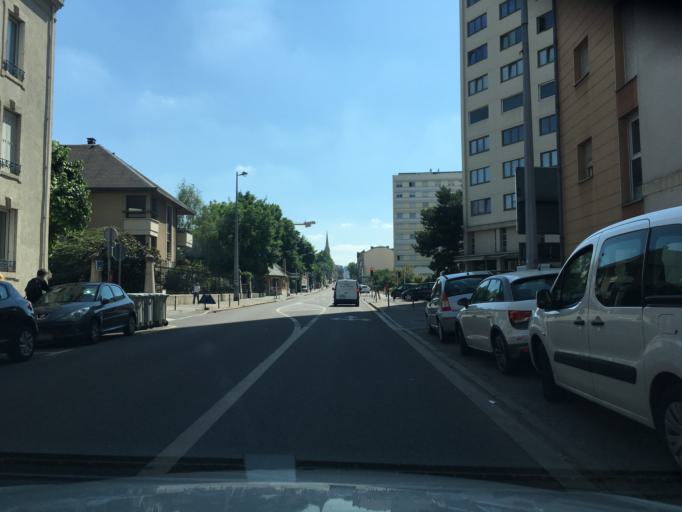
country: FR
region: Lorraine
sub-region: Departement de Meurthe-et-Moselle
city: Nancy
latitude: 48.6807
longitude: 6.1822
